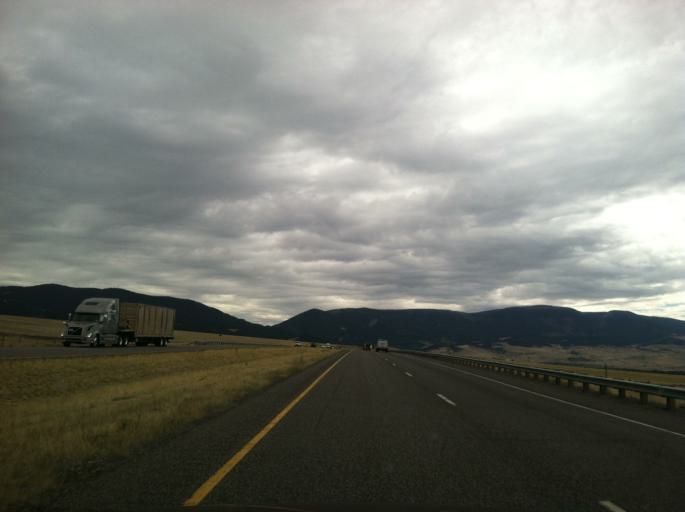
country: US
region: Montana
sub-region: Park County
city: Livingston
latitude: 45.6655
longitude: -110.5265
